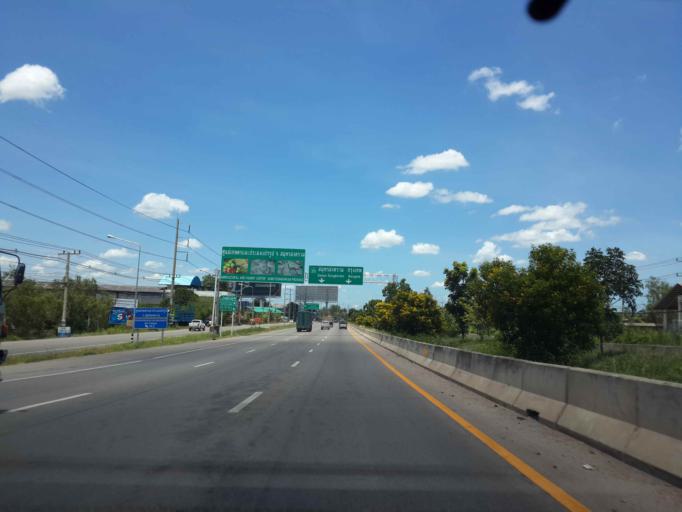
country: TH
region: Samut Songkhram
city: Amphawa
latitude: 13.3797
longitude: 99.9694
